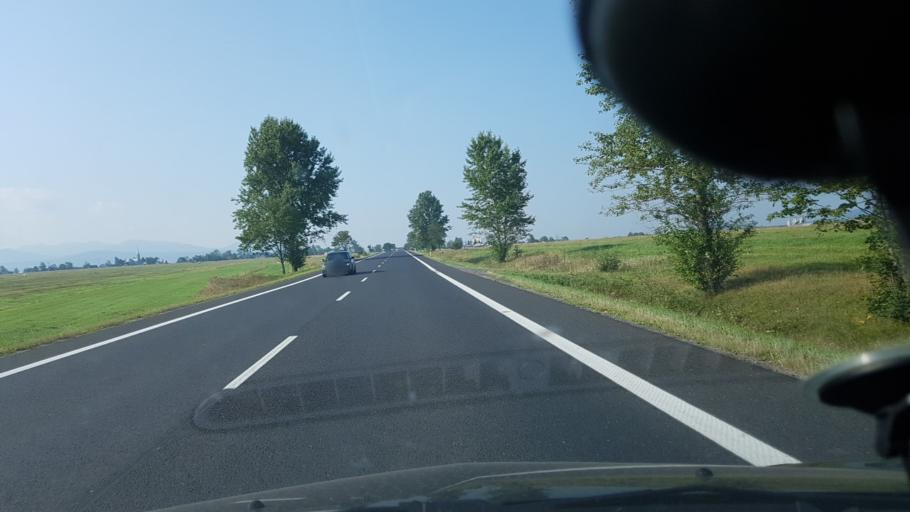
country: PL
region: Lesser Poland Voivodeship
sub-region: Powiat nowotarski
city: Chyzne
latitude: 49.4358
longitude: 19.6796
